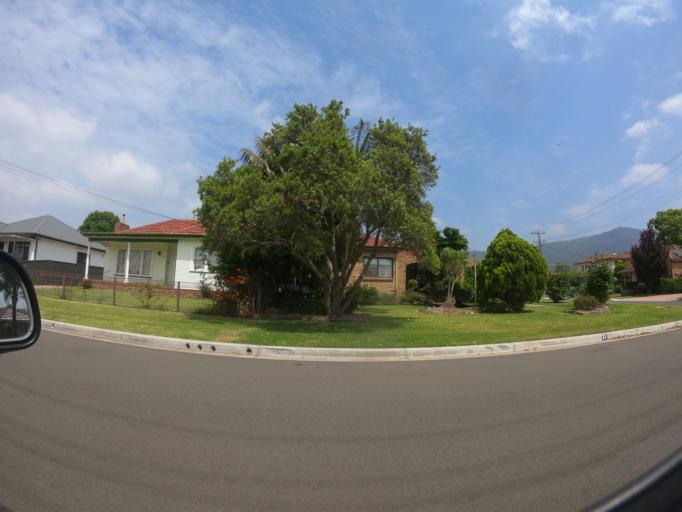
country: AU
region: New South Wales
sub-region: Wollongong
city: Fairy Meadow
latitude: -34.3850
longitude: 150.8866
